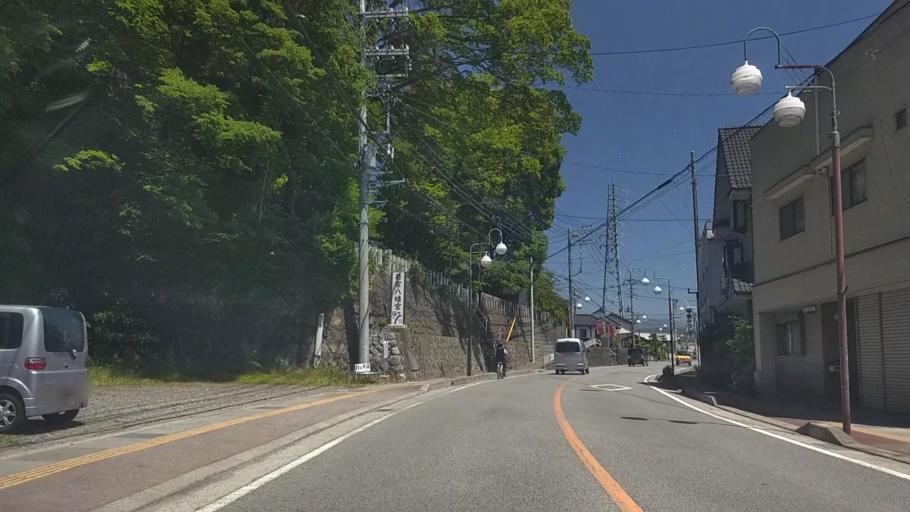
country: JP
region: Yamanashi
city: Nirasaki
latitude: 35.7139
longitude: 138.4482
